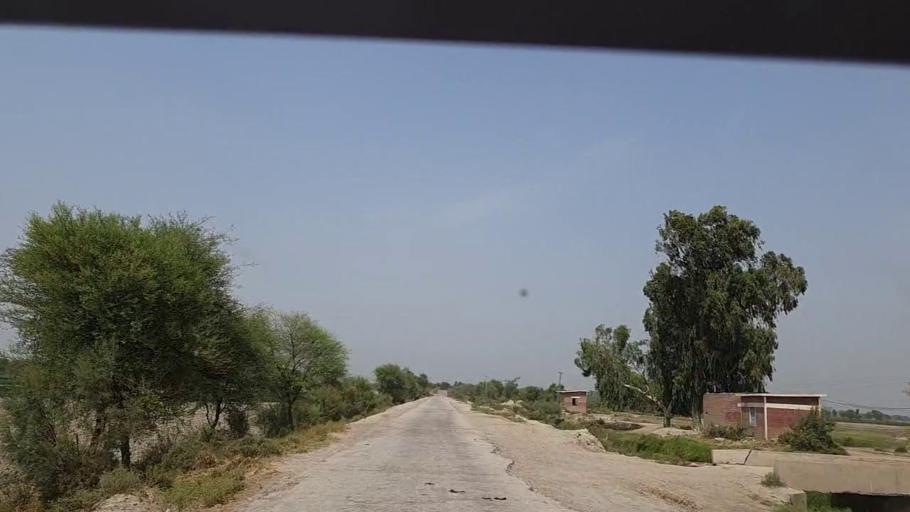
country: PK
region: Sindh
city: Khairpur Nathan Shah
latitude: 27.0776
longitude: 67.6544
